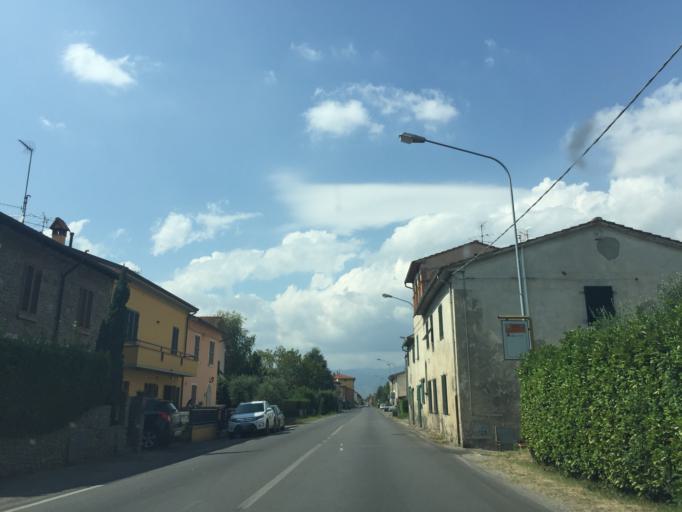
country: IT
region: Tuscany
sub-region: Provincia di Pistoia
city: Barba
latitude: 43.8969
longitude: 10.9540
